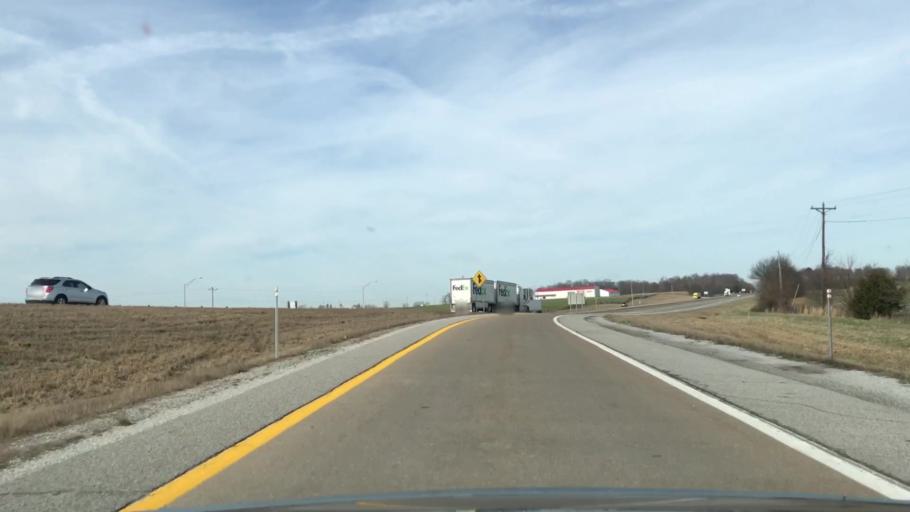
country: US
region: Kentucky
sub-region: Trigg County
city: Cadiz
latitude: 36.8847
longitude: -87.7348
